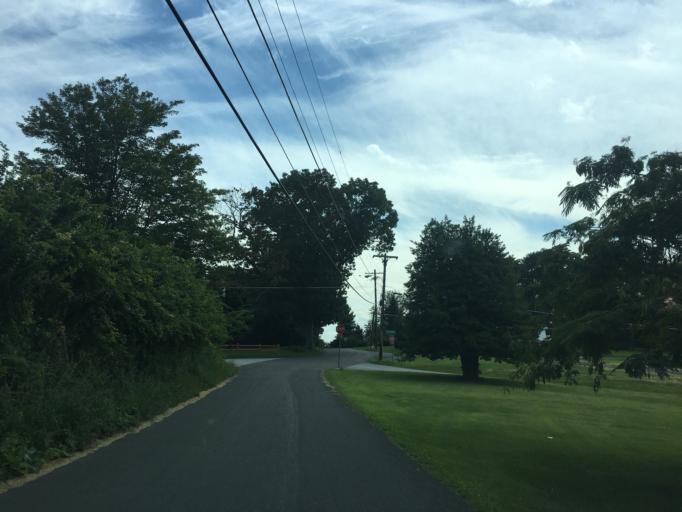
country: US
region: Pennsylvania
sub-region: York County
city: New Freedom
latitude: 39.6797
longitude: -76.6585
